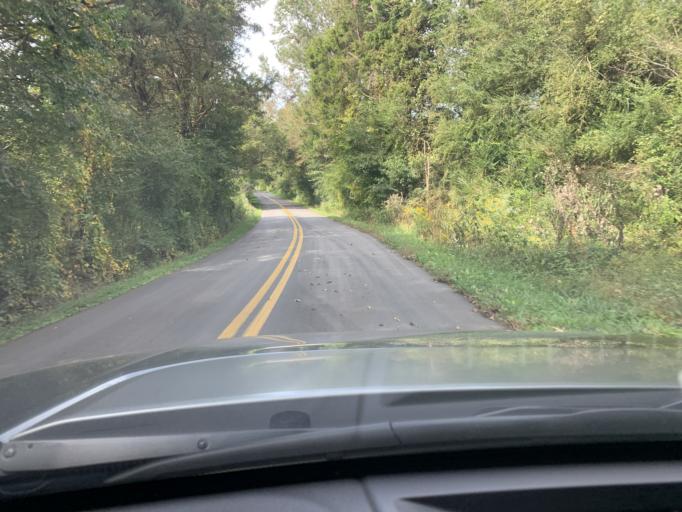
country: US
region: Georgia
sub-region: Floyd County
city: Cave Spring
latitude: 33.9490
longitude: -85.3830
